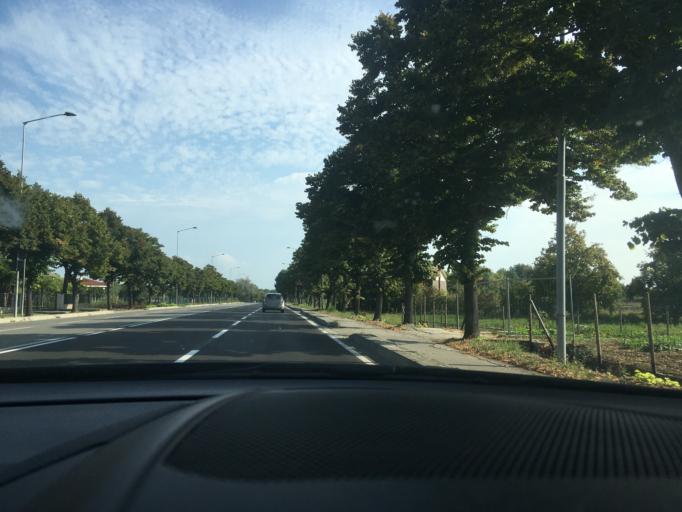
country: IT
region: Emilia-Romagna
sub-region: Provincia di Rimini
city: Santa Giustina
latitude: 44.1070
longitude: 12.4968
